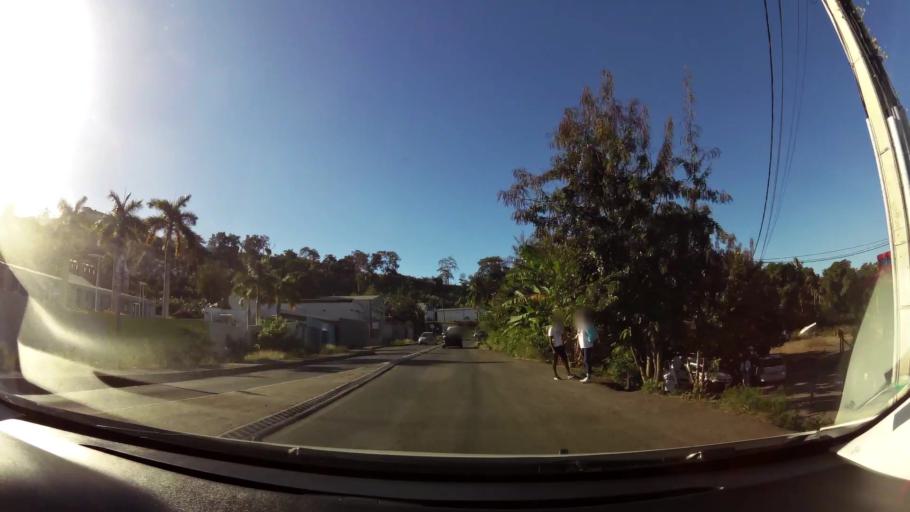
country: YT
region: Mamoudzou
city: Mamoudzou
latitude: -12.7611
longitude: 45.2264
